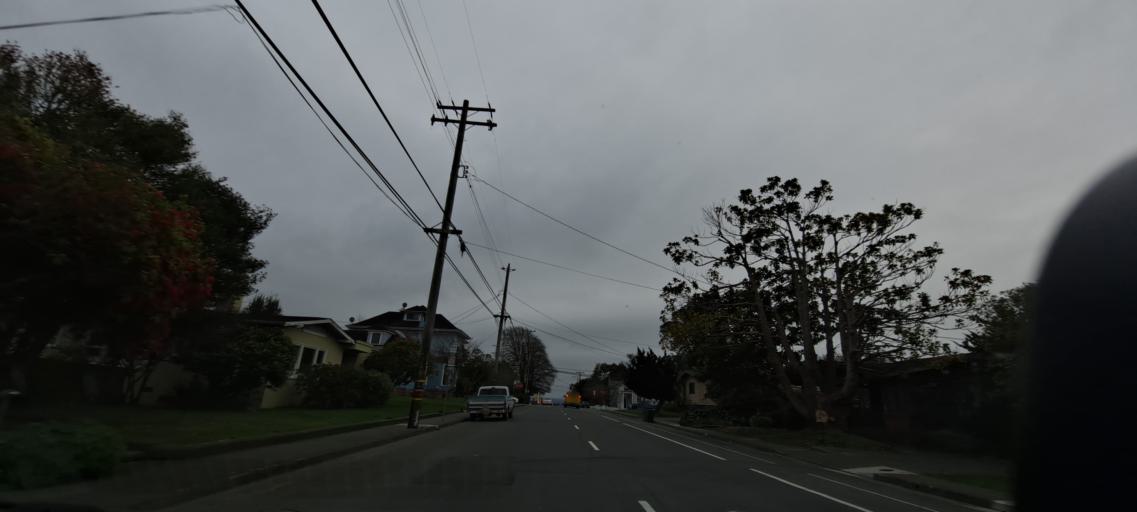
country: US
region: California
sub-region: Humboldt County
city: Arcata
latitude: 40.8737
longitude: -124.0851
